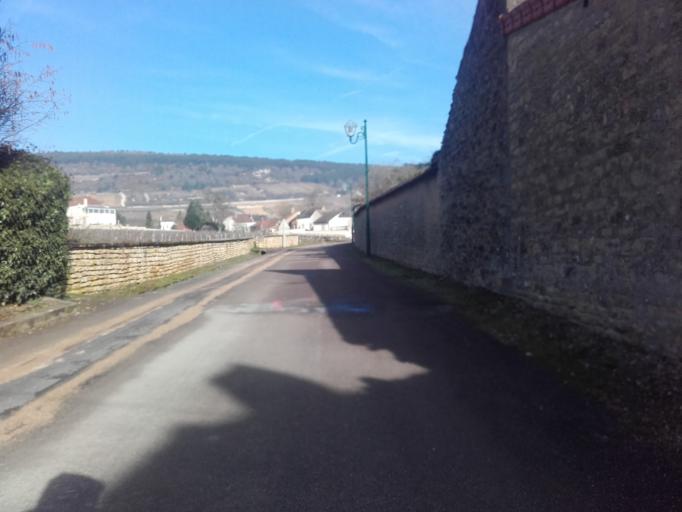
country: FR
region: Bourgogne
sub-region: Departement de Saone-et-Loire
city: Chagny
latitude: 46.9085
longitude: 4.6947
